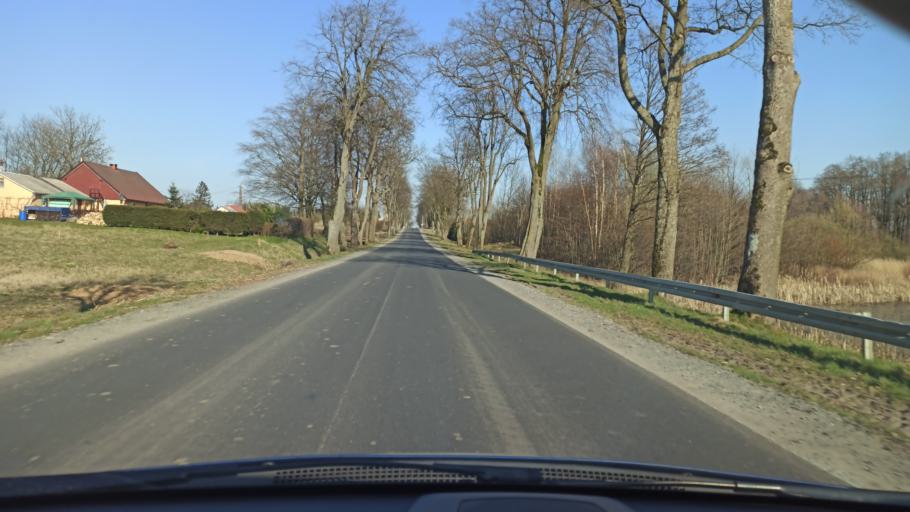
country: PL
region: Warmian-Masurian Voivodeship
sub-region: Powiat elblaski
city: Gronowo Gorne
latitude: 54.2158
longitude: 19.5240
